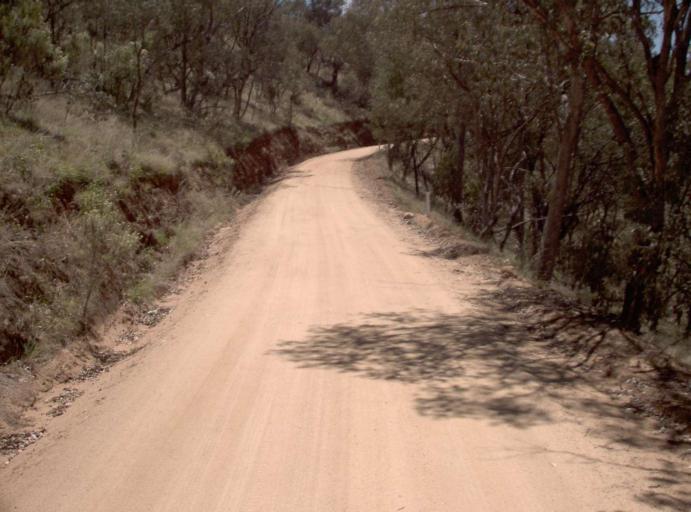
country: AU
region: New South Wales
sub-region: Snowy River
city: Jindabyne
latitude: -36.9365
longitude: 148.3627
